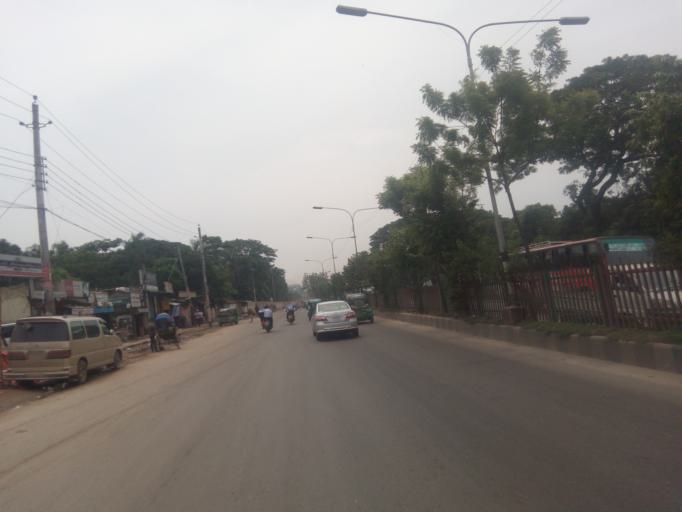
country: BD
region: Dhaka
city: Azimpur
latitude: 23.7805
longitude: 90.3538
